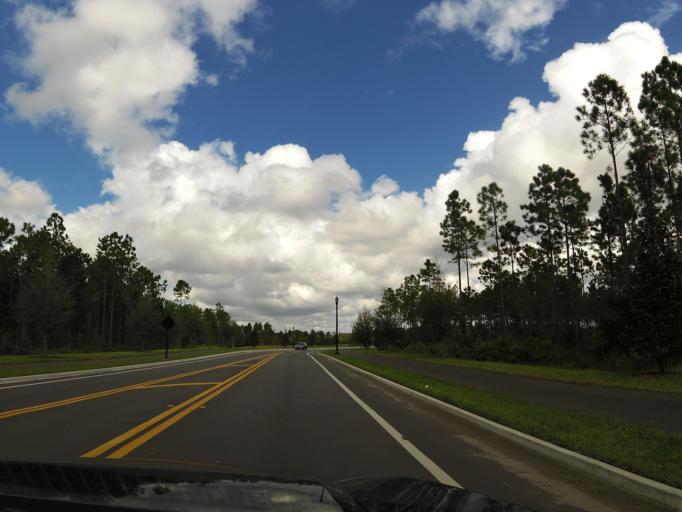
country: US
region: Florida
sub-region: Saint Johns County
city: Palm Valley
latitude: 30.0524
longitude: -81.3963
